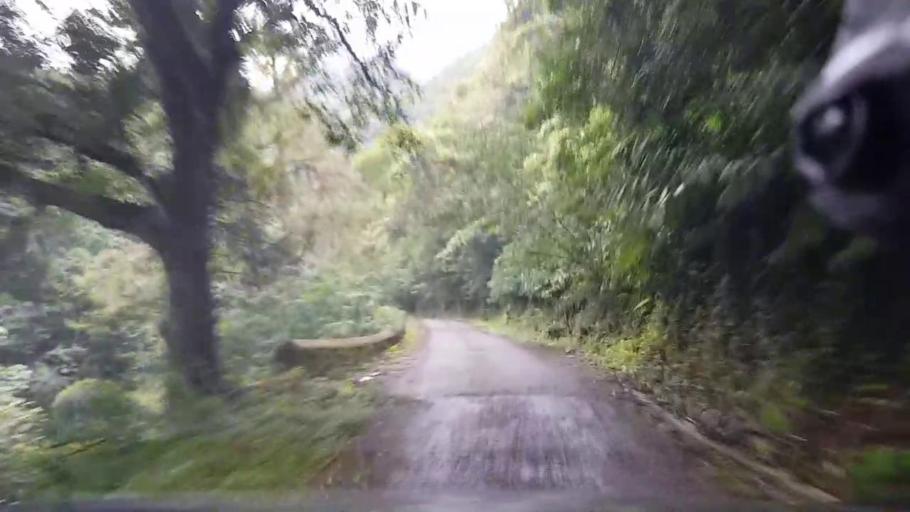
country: JM
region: Saint Andrew
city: Gordon Town
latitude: 18.1063
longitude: -76.7163
